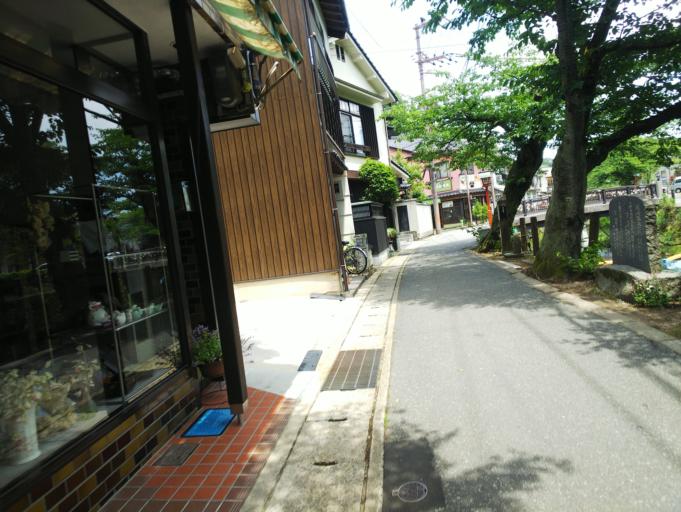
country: JP
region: Hyogo
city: Toyooka
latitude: 35.6256
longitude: 134.8086
